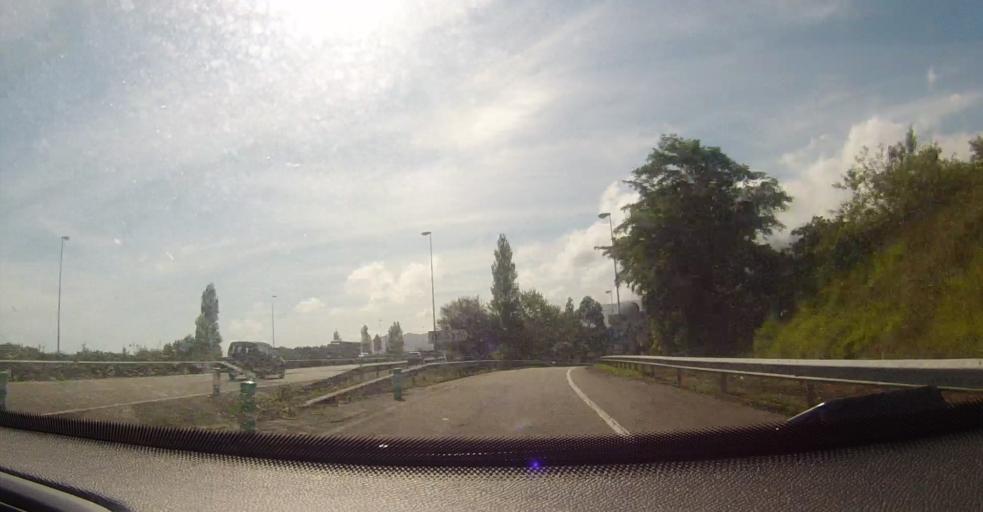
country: ES
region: Asturias
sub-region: Province of Asturias
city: Colunga
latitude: 43.4807
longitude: -5.2569
